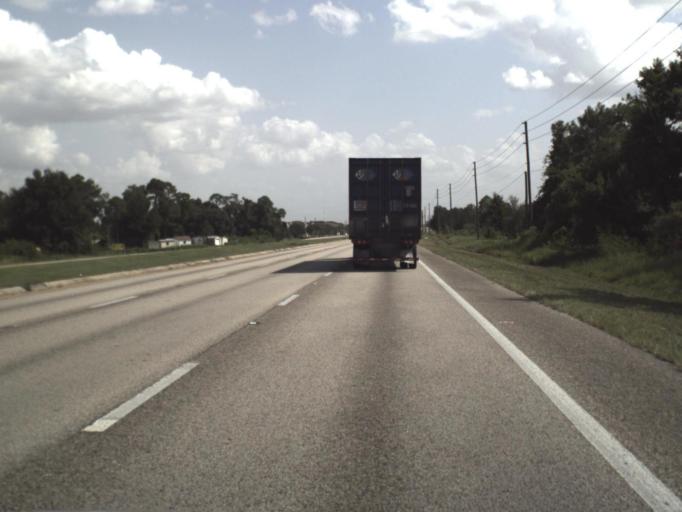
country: US
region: Florida
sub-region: Polk County
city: Lake Wales
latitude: 27.9378
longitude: -81.6119
